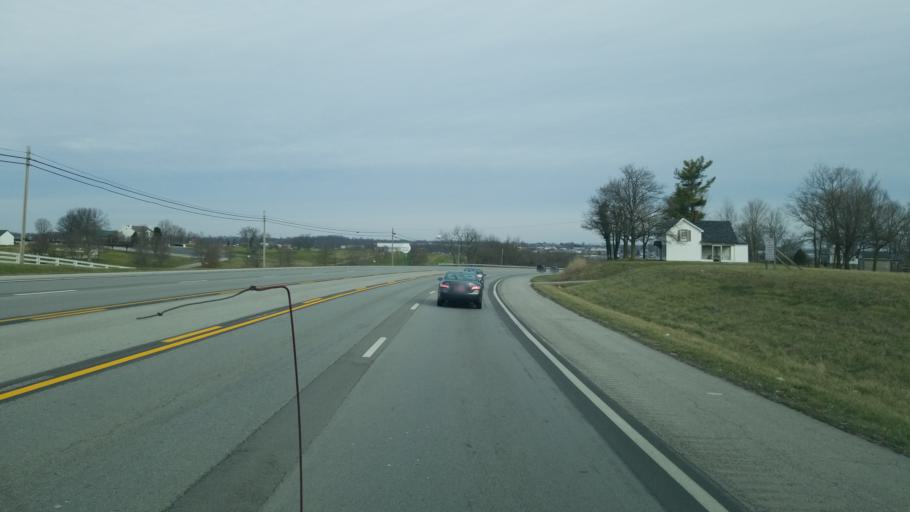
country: US
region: Kentucky
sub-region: Jessamine County
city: Nicholasville
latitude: 37.9214
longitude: -84.5554
